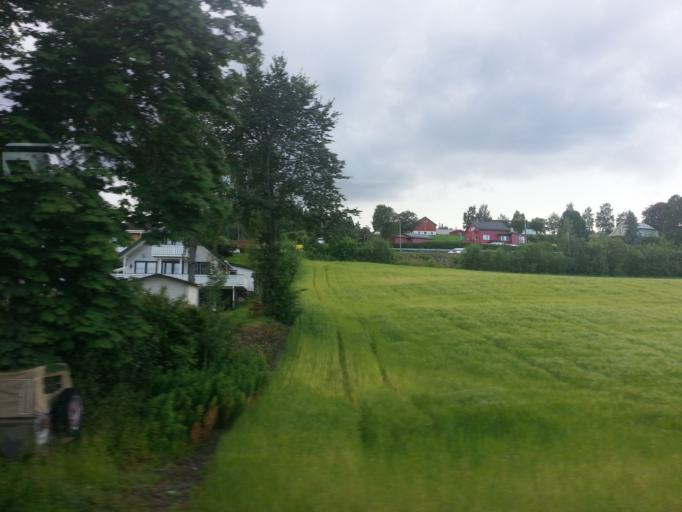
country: NO
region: Sor-Trondelag
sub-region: Malvik
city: Malvik
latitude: 63.4394
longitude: 10.6582
